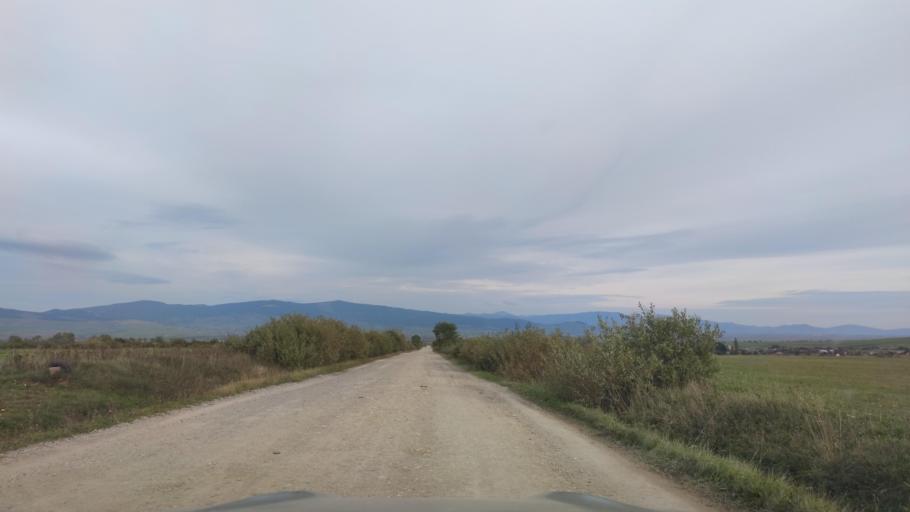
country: RO
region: Harghita
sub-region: Comuna Remetea
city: Remetea
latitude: 46.8110
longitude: 25.3902
